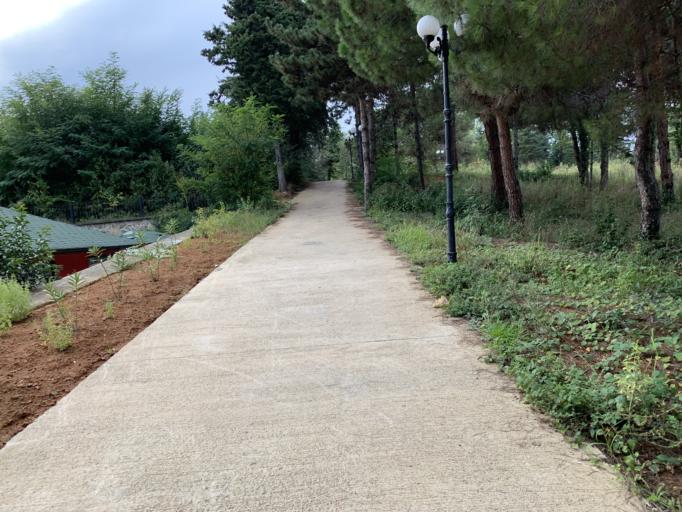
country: TR
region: Trabzon
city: Trabzon
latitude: 40.9897
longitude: 39.7702
